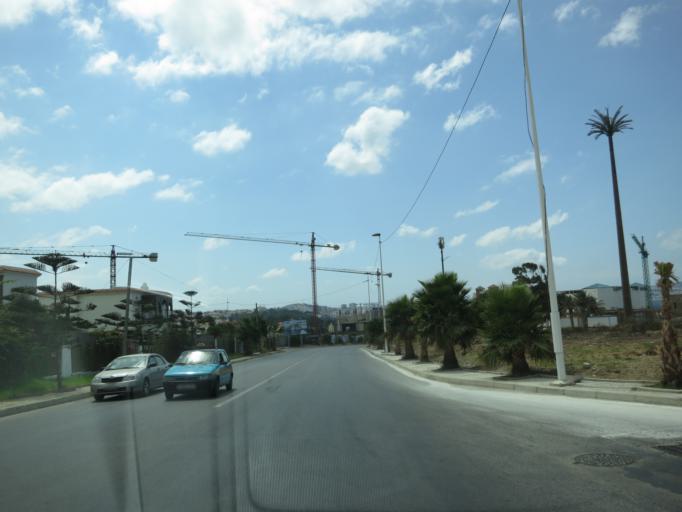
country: MA
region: Tanger-Tetouan
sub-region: Tanger-Assilah
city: Tangier
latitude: 35.7880
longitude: -5.7569
